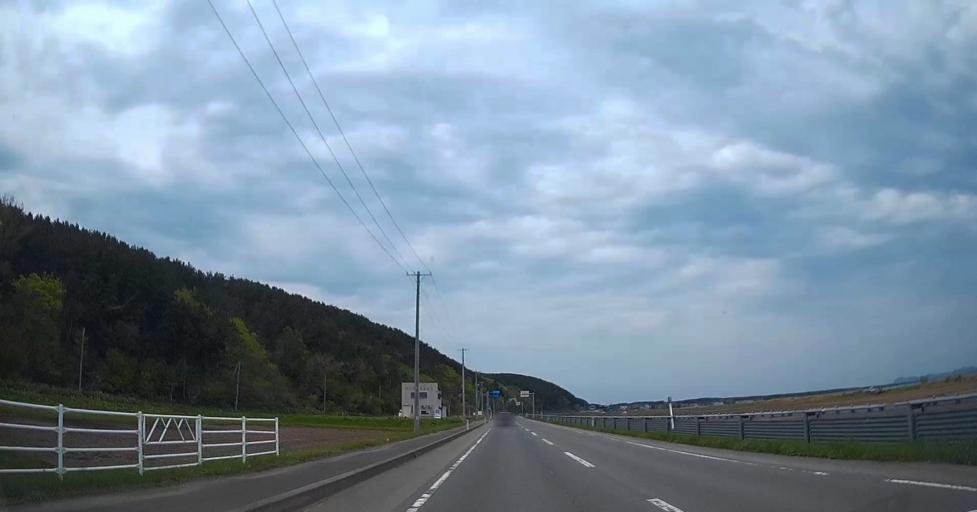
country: JP
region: Aomori
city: Shimokizukuri
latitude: 40.9944
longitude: 140.3557
